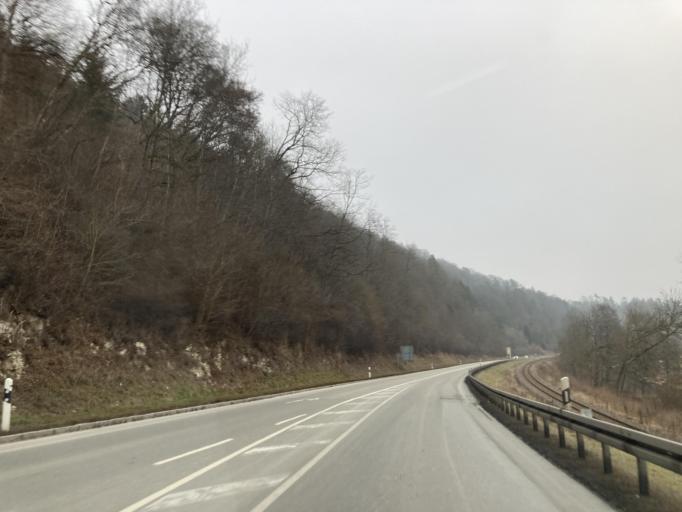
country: DE
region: Baden-Wuerttemberg
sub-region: Freiburg Region
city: Immendingen
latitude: 47.9392
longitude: 8.7413
